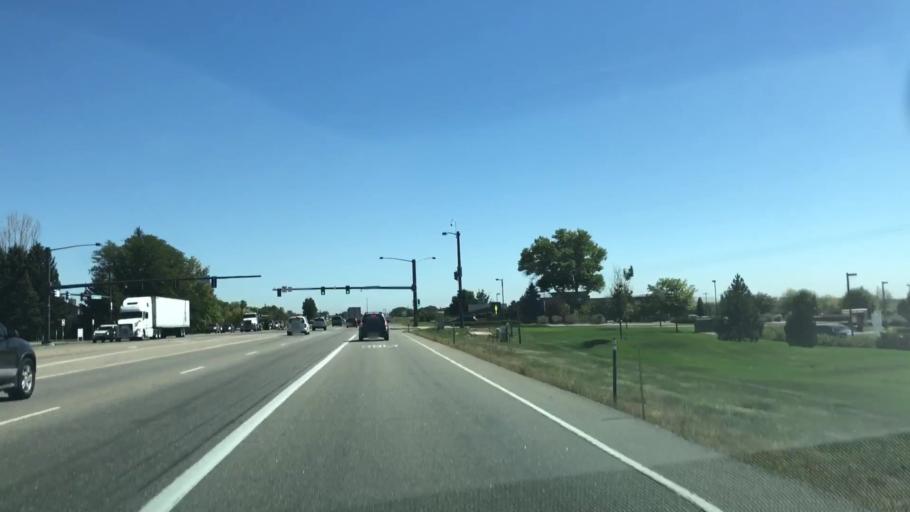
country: US
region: Colorado
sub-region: Weld County
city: Johnstown
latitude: 40.4071
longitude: -104.9751
